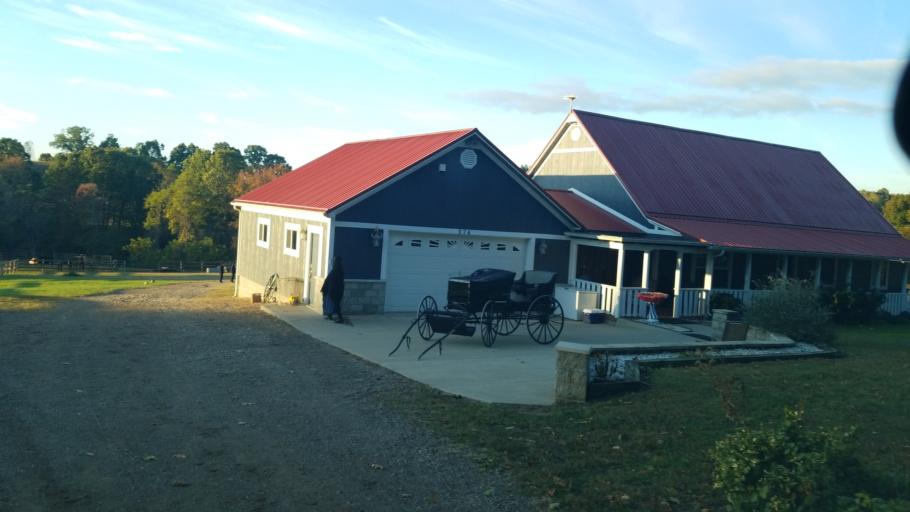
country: US
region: Ohio
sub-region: Jackson County
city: Wellston
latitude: 39.1672
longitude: -82.5495
